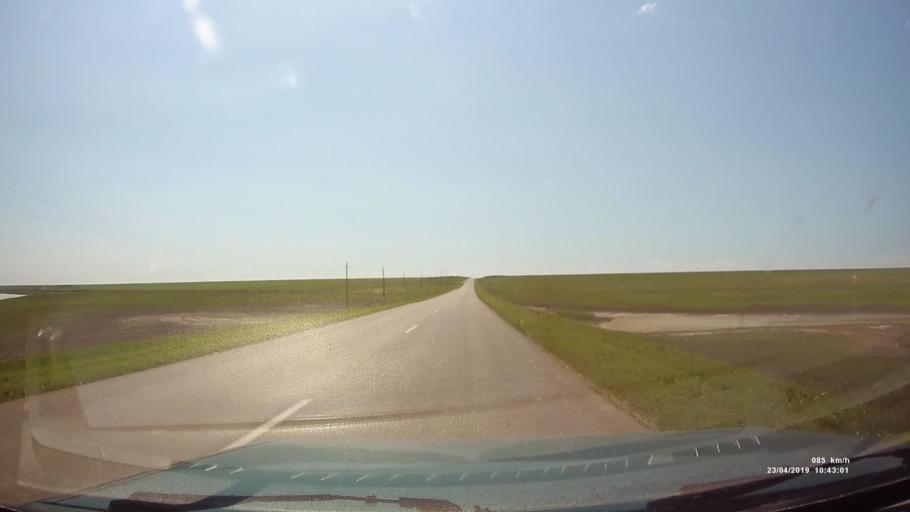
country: RU
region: Kalmykiya
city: Yashalta
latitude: 46.4751
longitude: 42.6480
